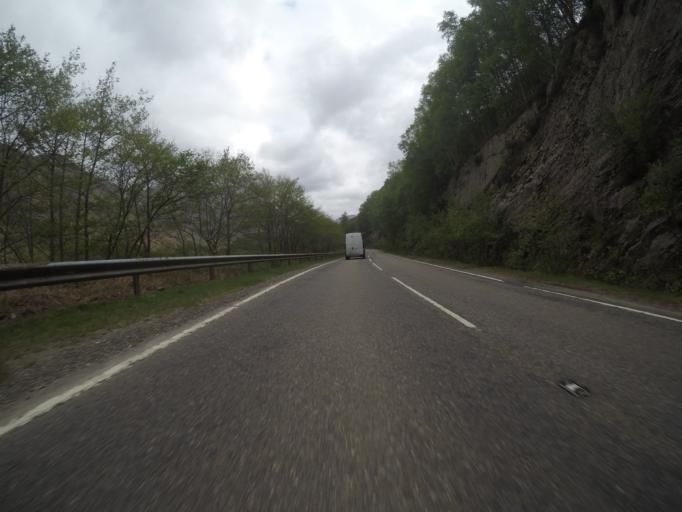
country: GB
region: Scotland
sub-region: Highland
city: Fort William
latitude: 57.2103
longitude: -5.4095
